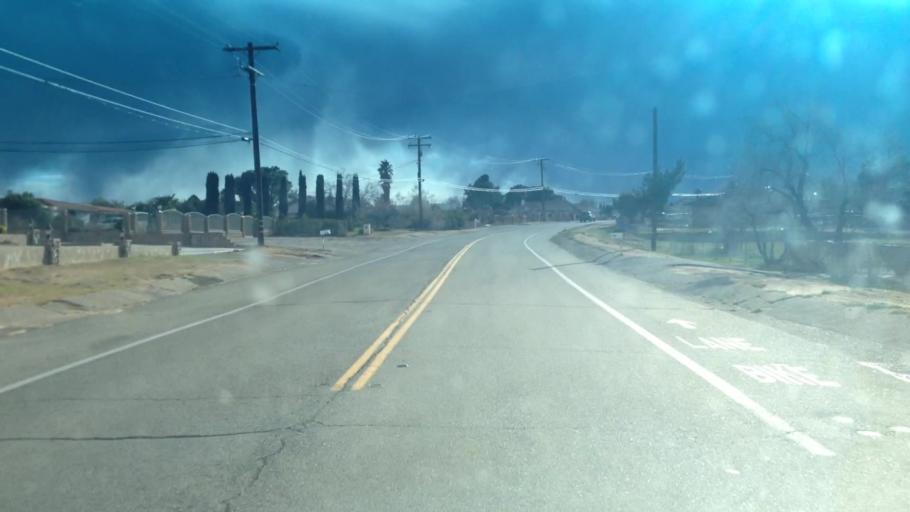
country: US
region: California
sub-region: San Bernardino County
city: Hesperia
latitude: 34.3891
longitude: -117.2560
